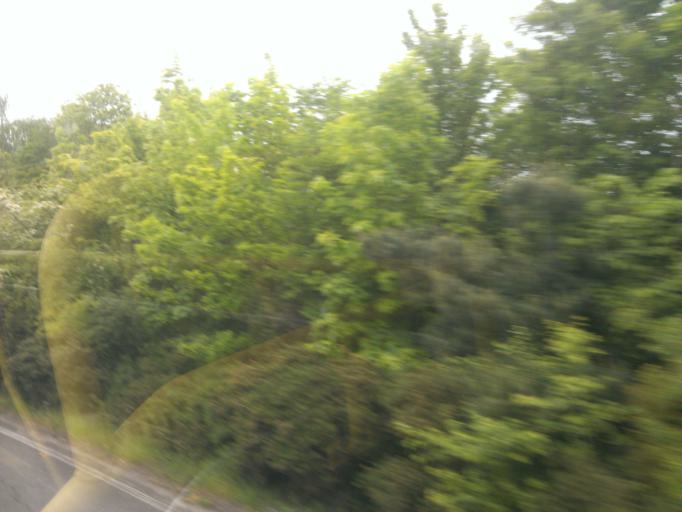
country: GB
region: England
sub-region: Essex
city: Colchester
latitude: 51.9249
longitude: 0.9374
